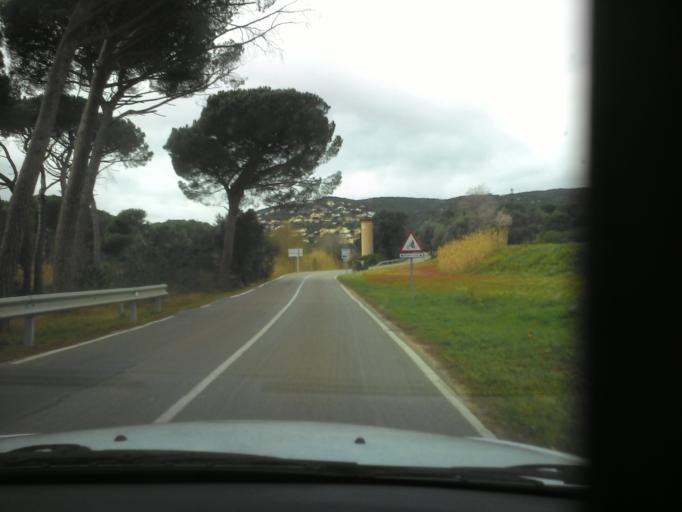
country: ES
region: Catalonia
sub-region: Provincia de Girona
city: Calonge
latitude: 41.8581
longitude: 3.0715
